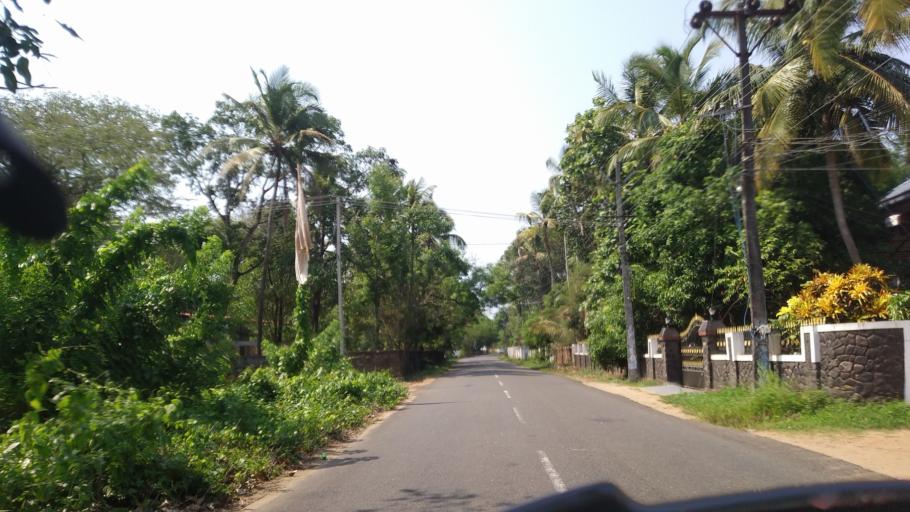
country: IN
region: Kerala
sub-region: Thrissur District
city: Irinjalakuda
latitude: 10.3247
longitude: 76.1233
